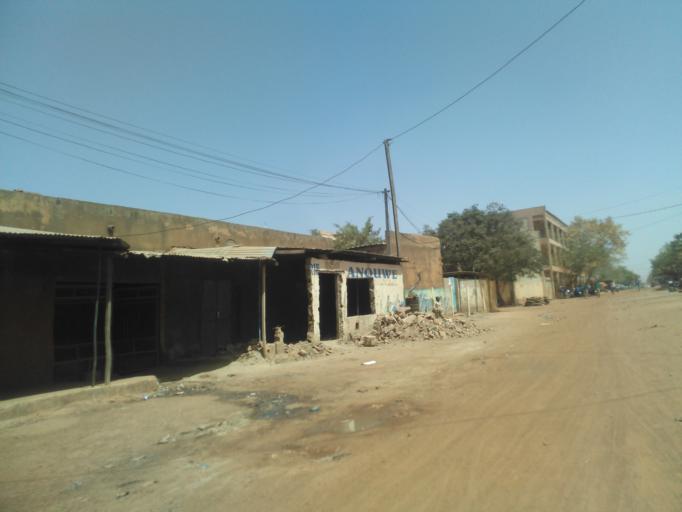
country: BF
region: Centre
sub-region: Kadiogo Province
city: Ouagadougou
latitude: 12.3920
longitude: -1.5648
